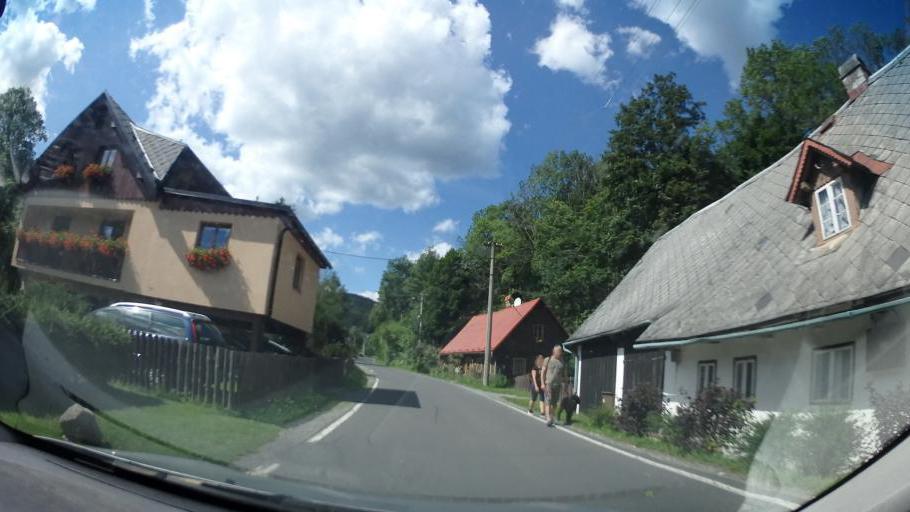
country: CZ
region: Olomoucky
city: Vapenna
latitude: 50.2253
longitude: 17.0904
